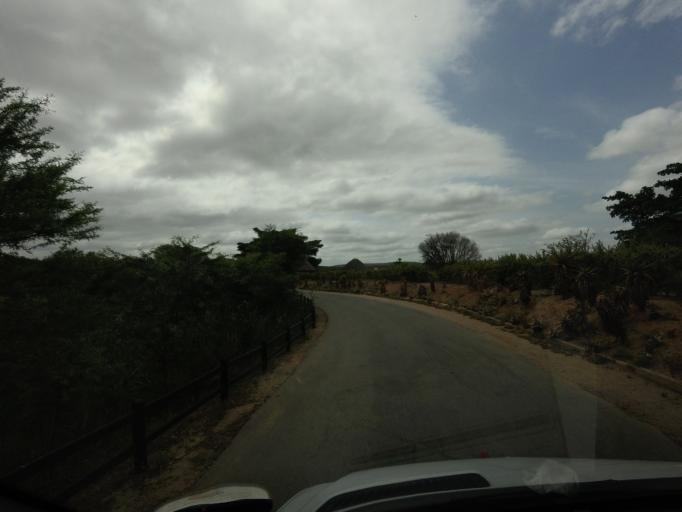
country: ZA
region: Eastern Cape
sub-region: Cacadu District Municipality
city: Kirkwood
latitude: -33.4447
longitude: 25.7469
